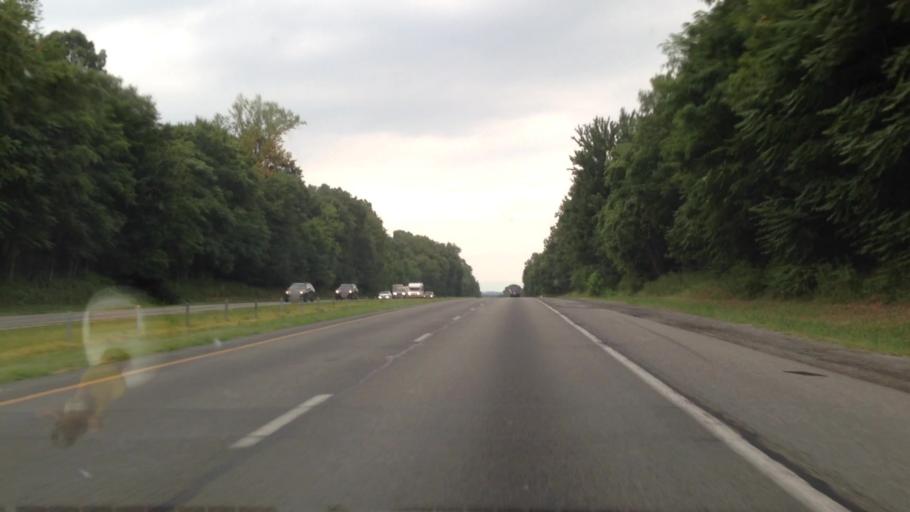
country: US
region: North Carolina
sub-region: Surry County
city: Pilot Mountain
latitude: 36.3487
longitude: -80.4653
